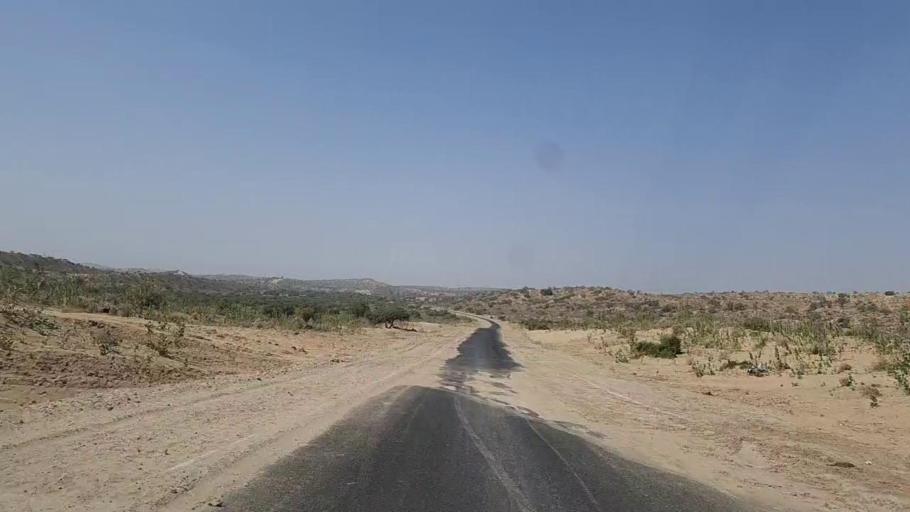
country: PK
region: Sindh
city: Diplo
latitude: 24.5804
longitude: 69.5090
